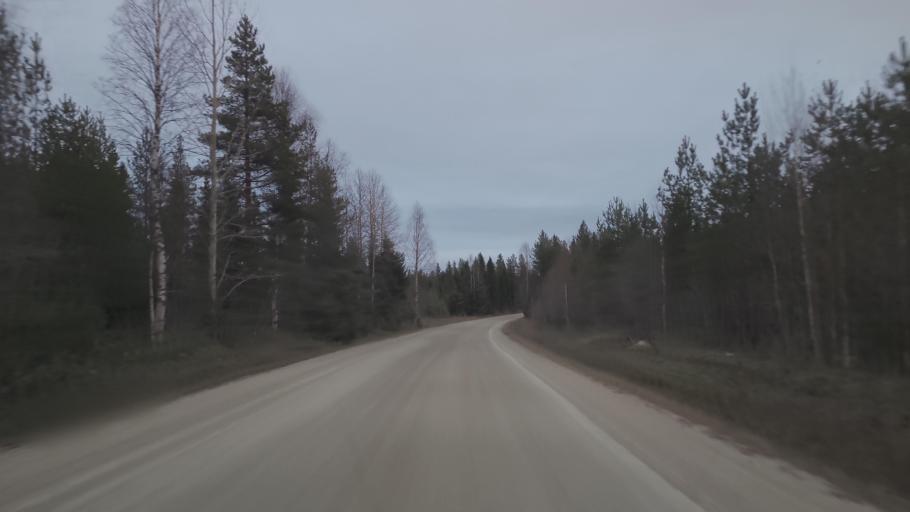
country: FI
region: Lapland
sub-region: Kemi-Tornio
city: Tervola
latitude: 66.0707
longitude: 24.8847
